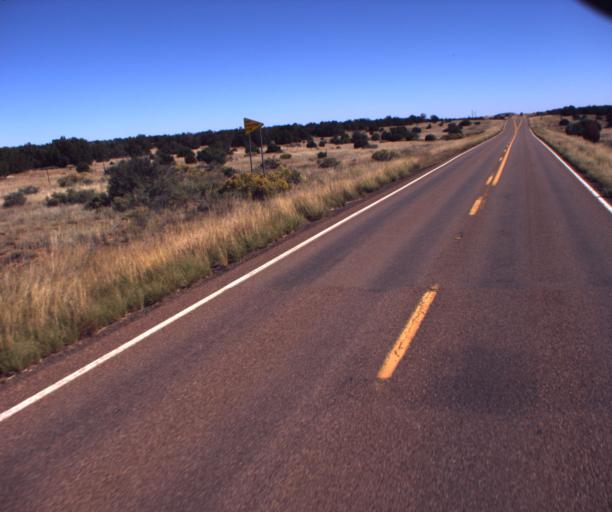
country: US
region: Arizona
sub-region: Navajo County
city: Heber-Overgaard
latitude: 34.4789
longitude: -110.3425
